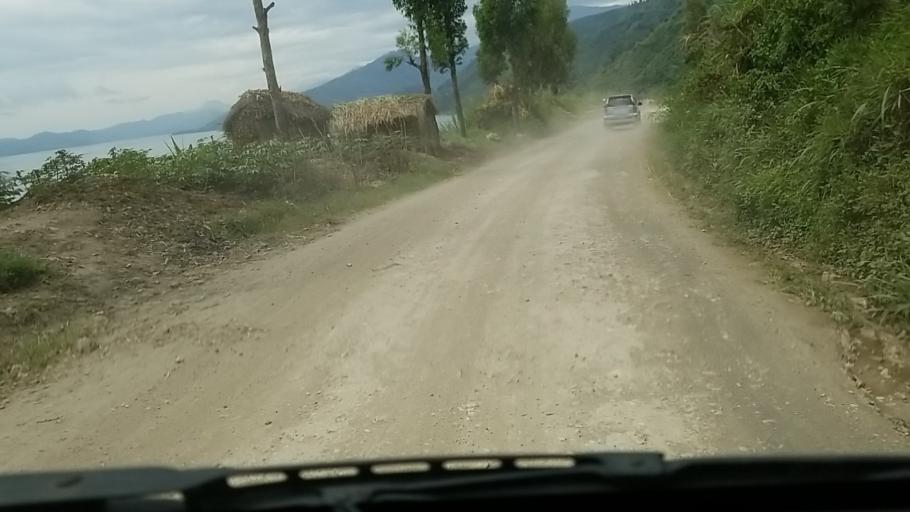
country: CD
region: Nord Kivu
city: Sake
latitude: -1.5896
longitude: 29.0457
